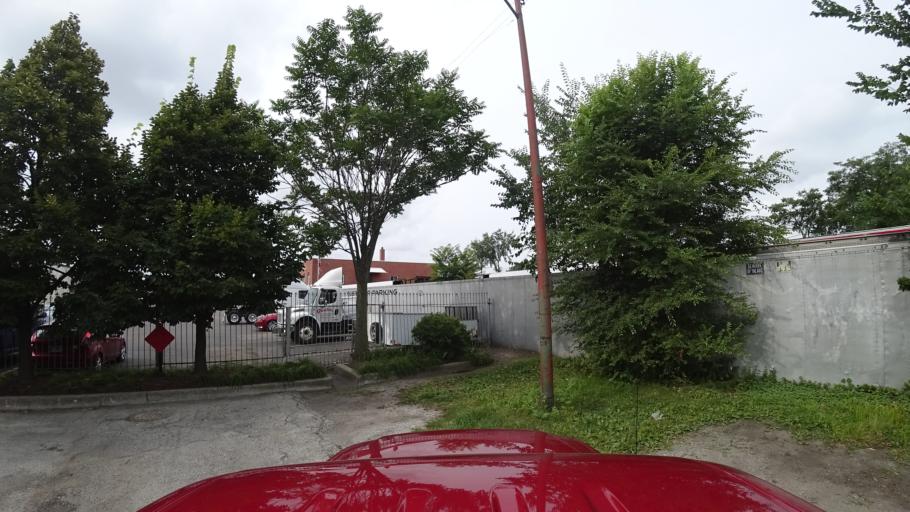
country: US
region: Illinois
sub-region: Cook County
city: Chicago
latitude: 41.8187
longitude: -87.6829
